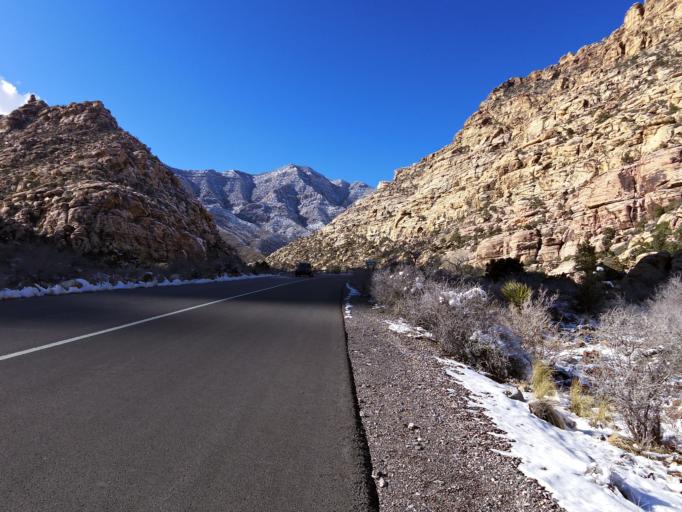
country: US
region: Nevada
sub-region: Clark County
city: Summerlin South
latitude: 36.1595
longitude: -115.4973
